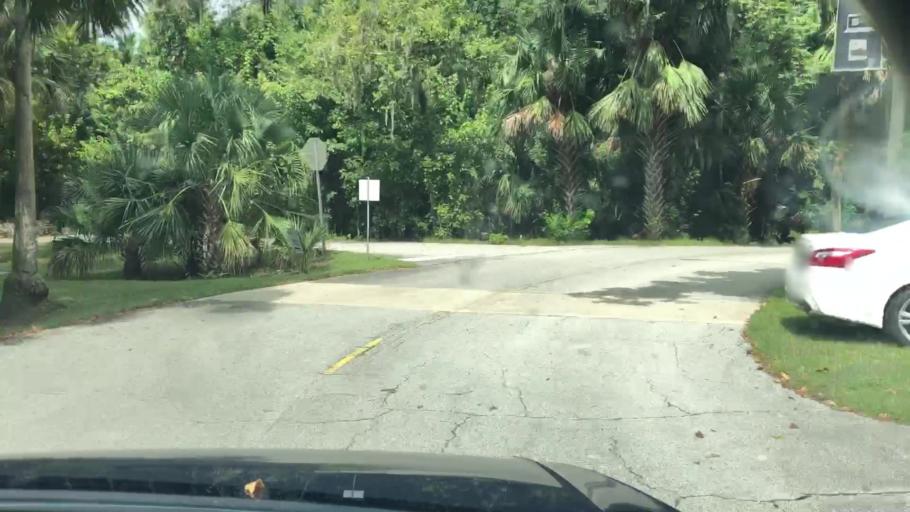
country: US
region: Florida
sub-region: Volusia County
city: Daytona Beach
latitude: 29.1930
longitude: -81.0373
